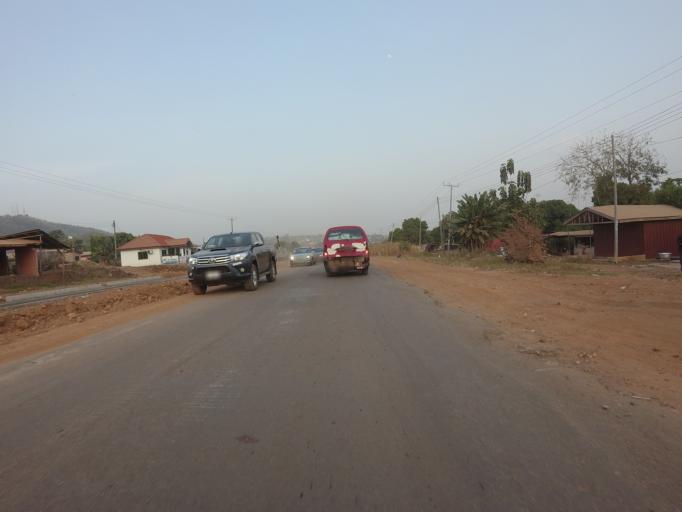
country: GH
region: Volta
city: Ho
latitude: 6.5933
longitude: 0.4368
